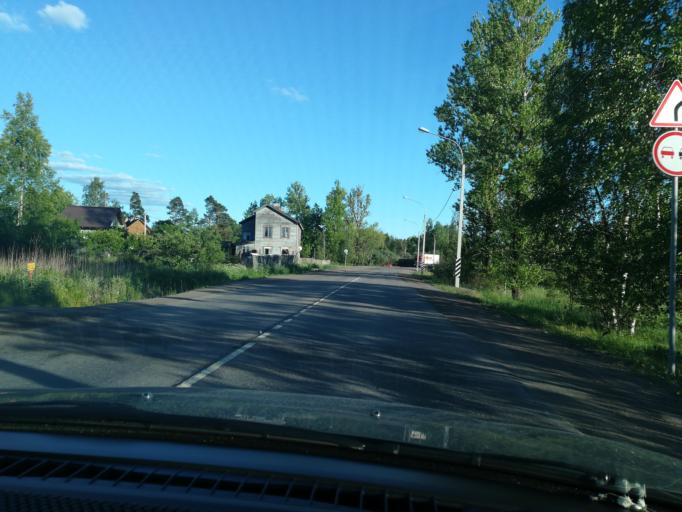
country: RU
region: Leningrad
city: Lesogorskiy
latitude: 61.0477
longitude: 28.9272
